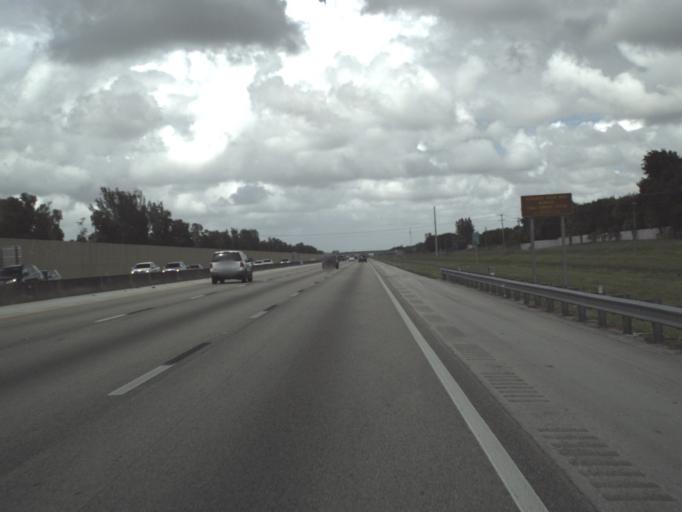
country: US
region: Florida
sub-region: Palm Beach County
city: Boca Del Mar
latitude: 26.3808
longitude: -80.1708
